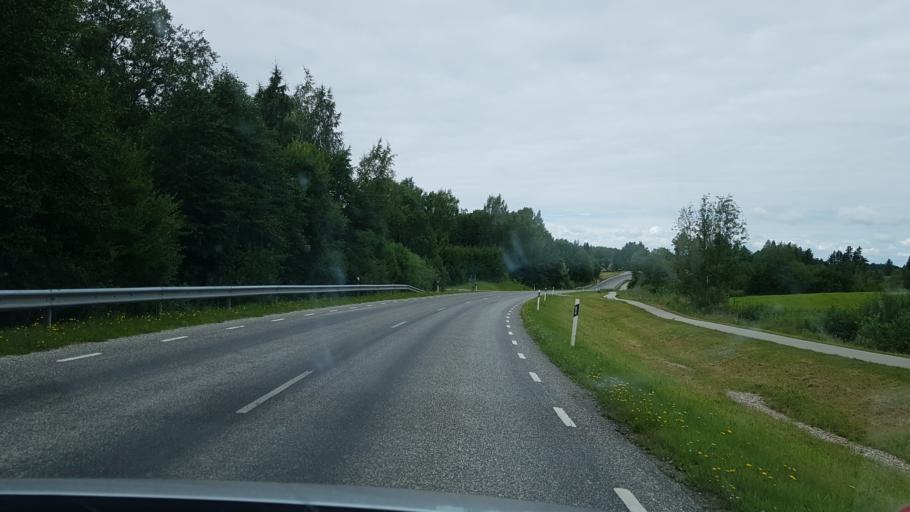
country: EE
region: Vorumaa
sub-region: Antsla vald
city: Vana-Antsla
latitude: 58.0498
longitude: 26.5410
